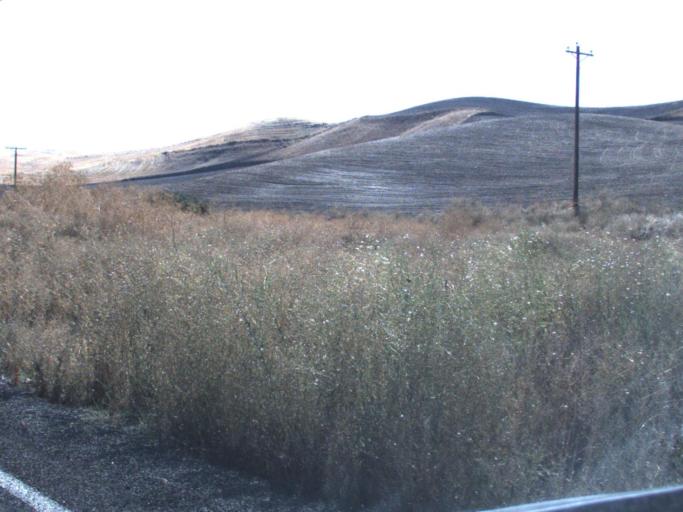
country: US
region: Washington
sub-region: Walla Walla County
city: Walla Walla
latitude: 46.2060
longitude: -118.3869
